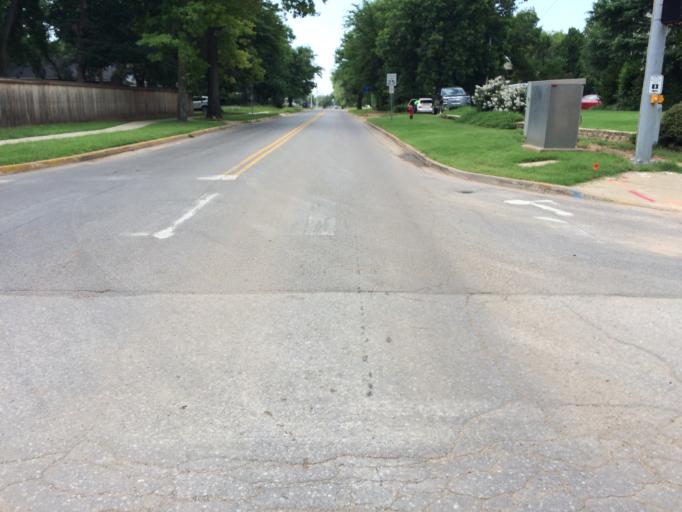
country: US
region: Oklahoma
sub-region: Cleveland County
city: Norman
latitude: 35.2039
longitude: -97.4502
